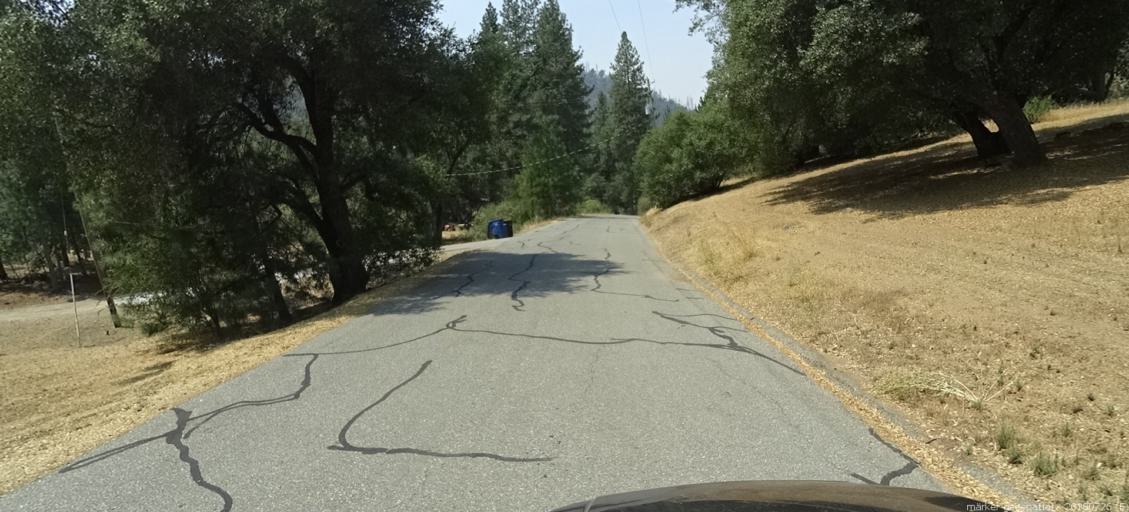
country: US
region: California
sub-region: Madera County
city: Oakhurst
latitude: 37.2839
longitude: -119.6470
